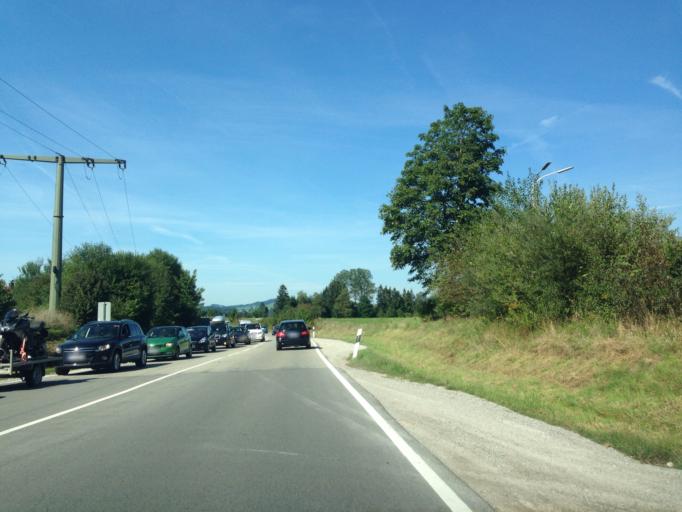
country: DE
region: Bavaria
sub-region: Swabia
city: Fuessen
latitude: 47.5834
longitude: 10.7068
